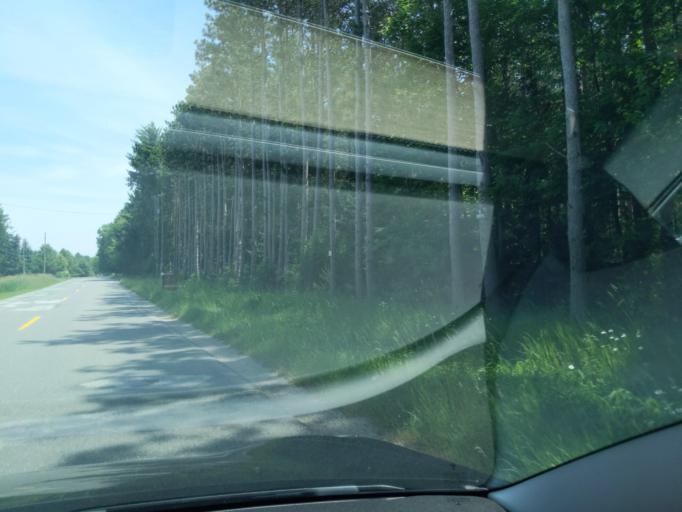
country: US
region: Michigan
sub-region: Muskegon County
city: Montague
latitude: 43.4160
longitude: -86.4118
